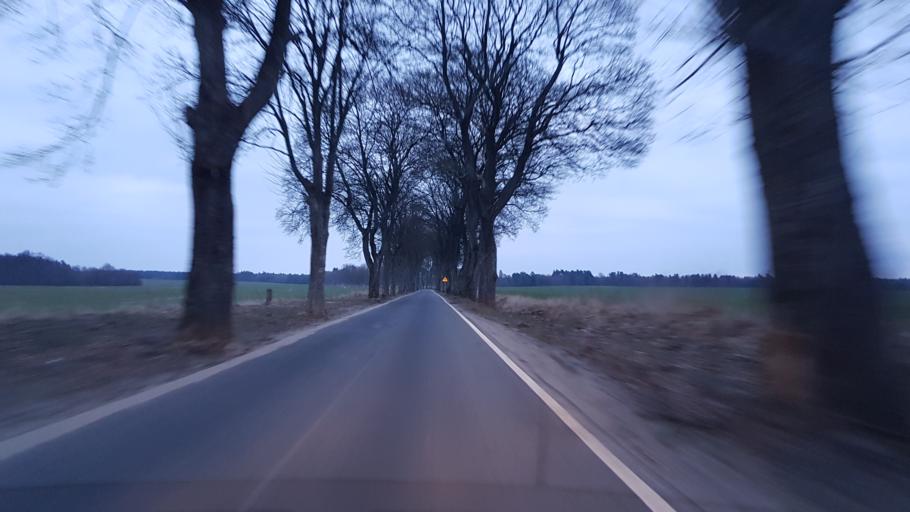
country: PL
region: Greater Poland Voivodeship
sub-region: Powiat zlotowski
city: Sypniewo
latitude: 53.4806
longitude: 16.6998
